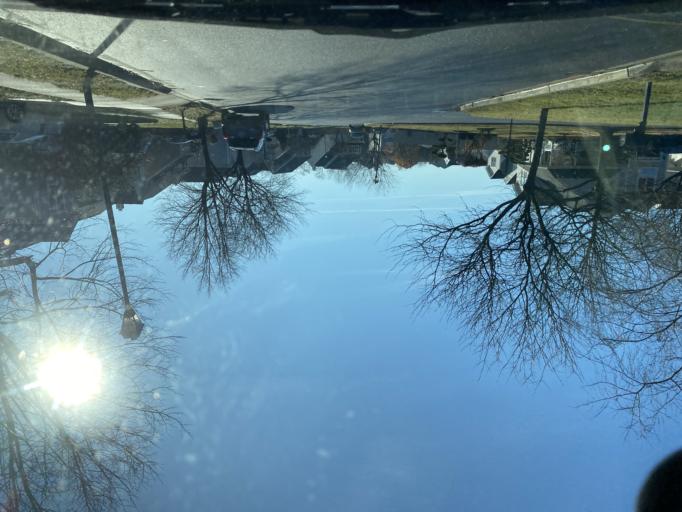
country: US
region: Maryland
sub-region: Prince George's County
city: South Laurel
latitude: 39.0817
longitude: -76.8704
